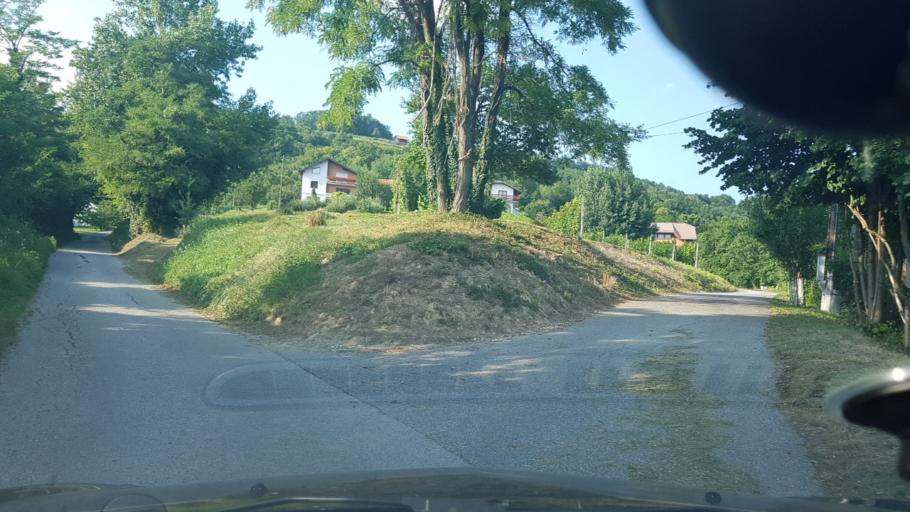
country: HR
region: Krapinsko-Zagorska
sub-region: Grad Krapina
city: Krapina
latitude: 46.1657
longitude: 15.8942
